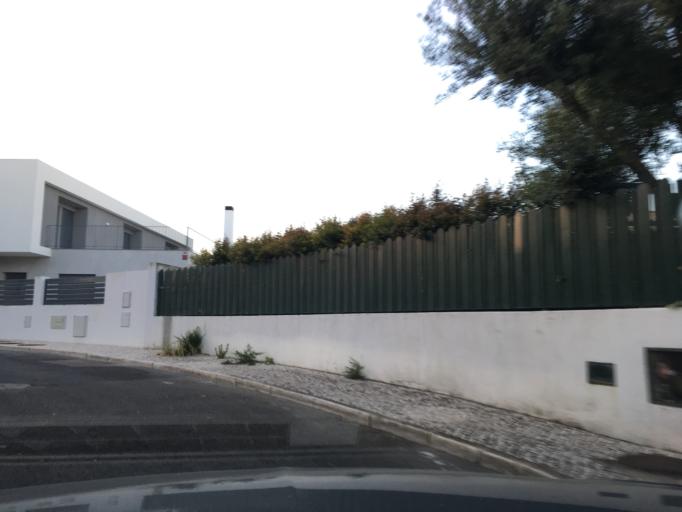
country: PT
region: Lisbon
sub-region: Oeiras
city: Barcarena
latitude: 38.7199
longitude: -9.2796
